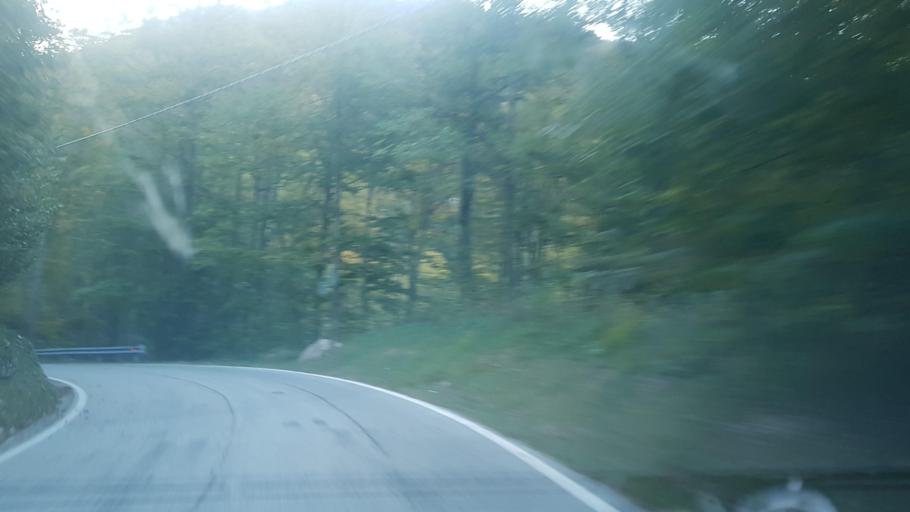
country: IT
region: Friuli Venezia Giulia
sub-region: Provincia di Udine
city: Villa Santina
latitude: 46.3504
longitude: 12.9188
